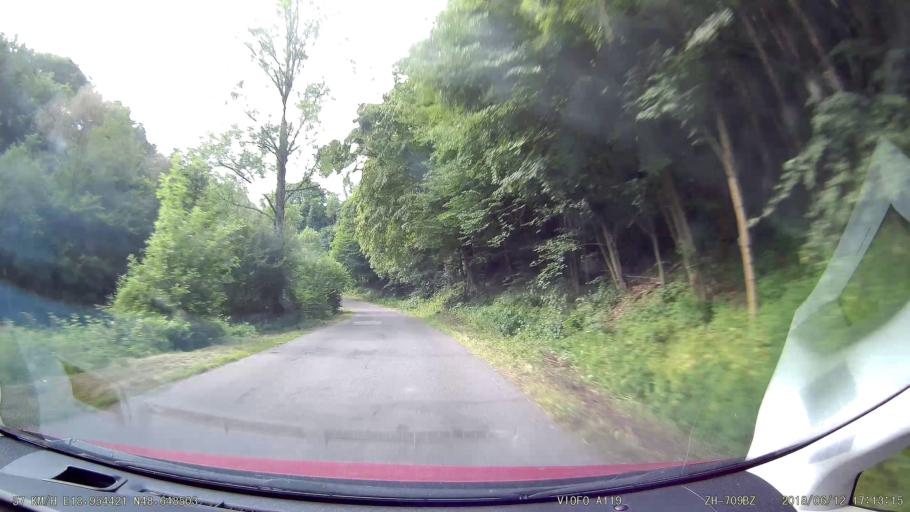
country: SK
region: Banskobystricky
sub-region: Okres Ziar nad Hronom
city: Kremnica
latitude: 48.6487
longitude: 18.9544
